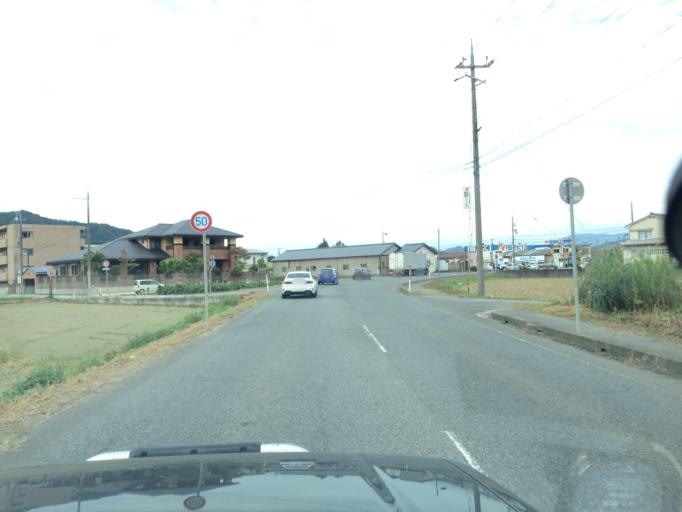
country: JP
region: Hyogo
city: Toyooka
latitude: 35.4924
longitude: 134.7991
